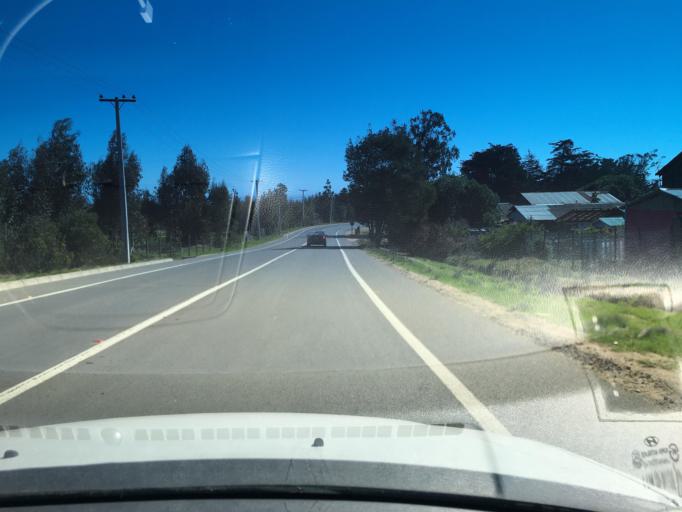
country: CL
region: Valparaiso
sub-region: San Antonio Province
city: El Tabo
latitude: -33.4257
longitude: -71.6714
